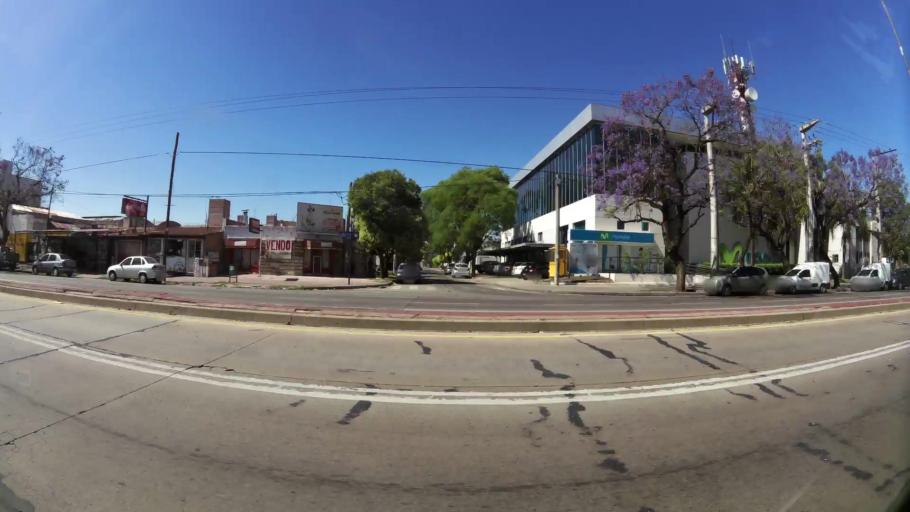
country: AR
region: Cordoba
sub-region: Departamento de Capital
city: Cordoba
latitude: -31.4330
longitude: -64.1501
